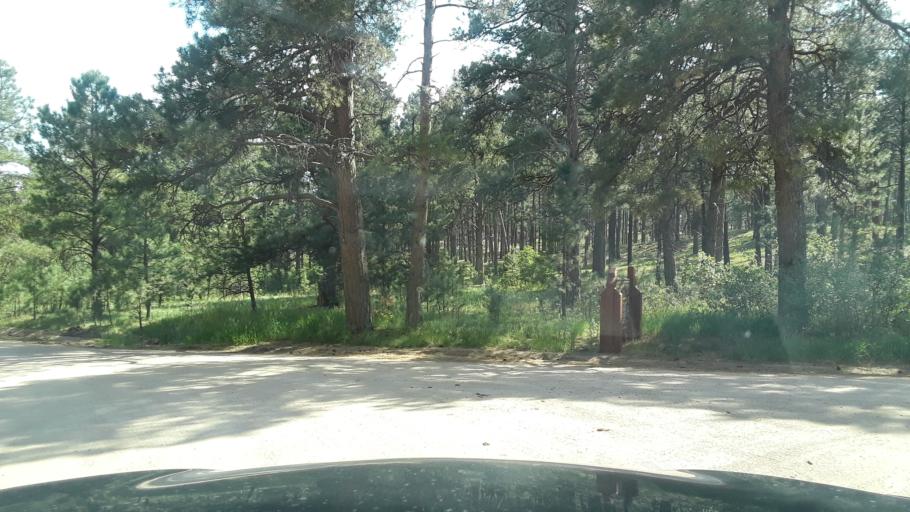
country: US
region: Colorado
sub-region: El Paso County
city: Gleneagle
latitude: 39.0601
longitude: -104.7932
